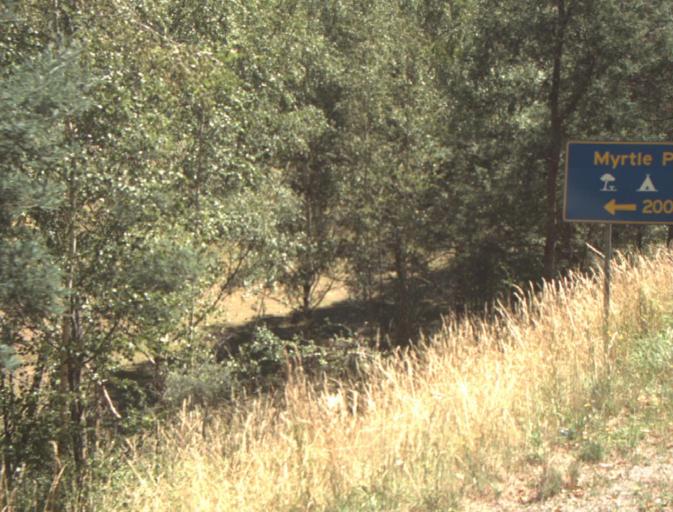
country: AU
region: Tasmania
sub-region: Dorset
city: Scottsdale
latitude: -41.3131
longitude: 147.3686
